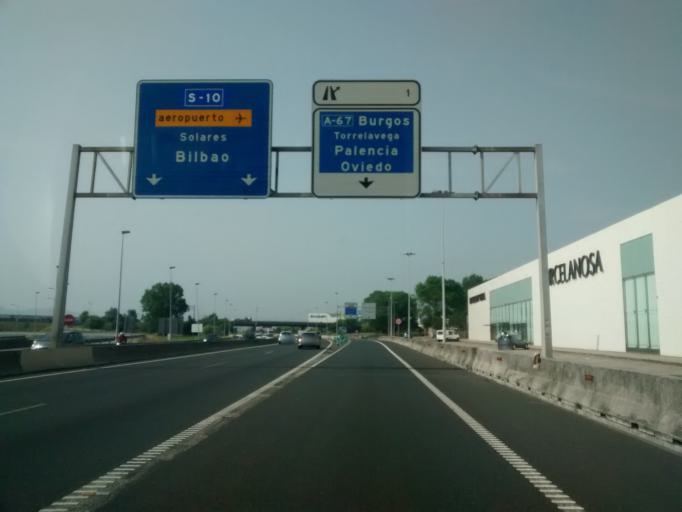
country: ES
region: Cantabria
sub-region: Provincia de Cantabria
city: Santander
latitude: 43.4433
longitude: -3.8351
